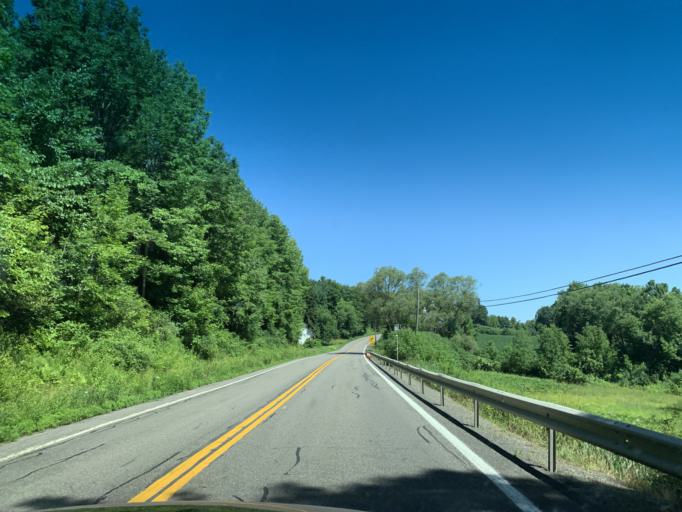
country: US
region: New York
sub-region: Chenango County
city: Norwich
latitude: 42.4799
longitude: -75.4054
